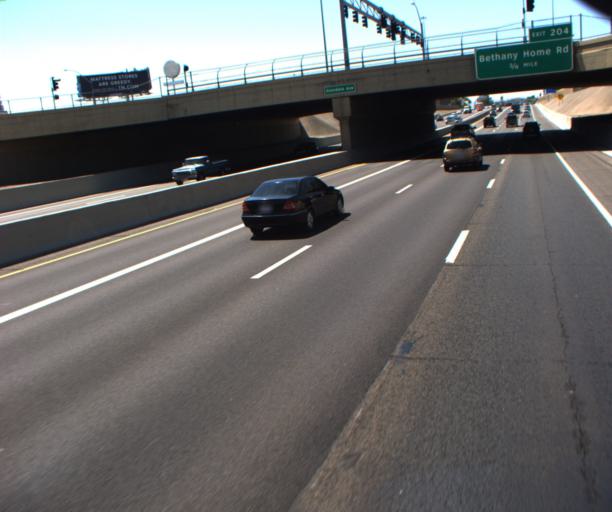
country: US
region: Arizona
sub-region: Maricopa County
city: Glendale
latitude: 33.5392
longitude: -112.1125
